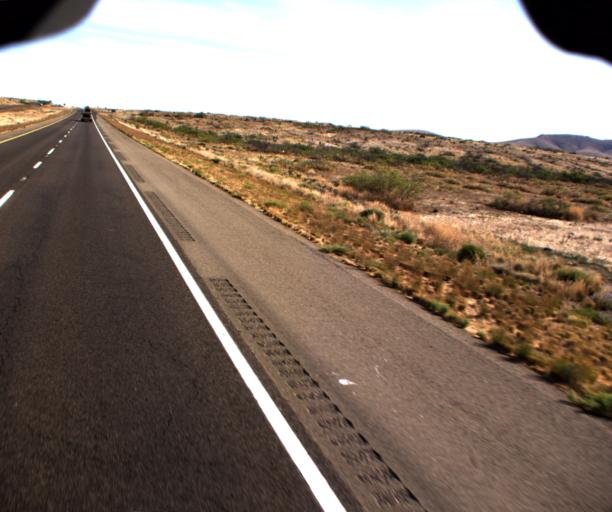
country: US
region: Arizona
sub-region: Cochise County
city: Willcox
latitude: 32.3882
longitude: -109.6654
